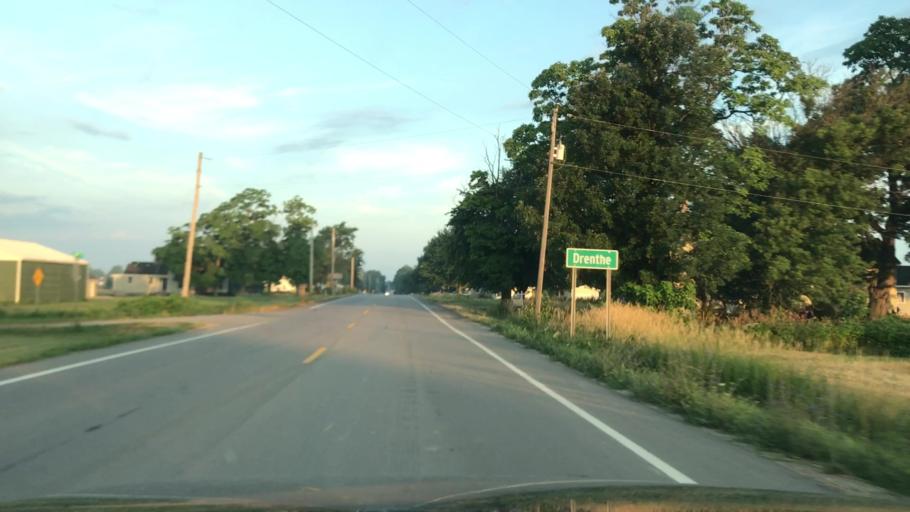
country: US
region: Michigan
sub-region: Ottawa County
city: Zeeland
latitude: 42.7827
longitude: -85.9301
